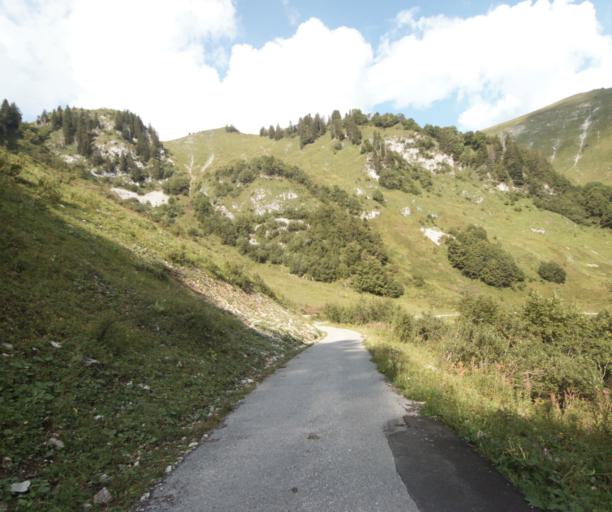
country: CH
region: Vaud
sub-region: Riviera-Pays-d'Enhaut District
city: Caux
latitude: 46.4253
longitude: 7.0002
